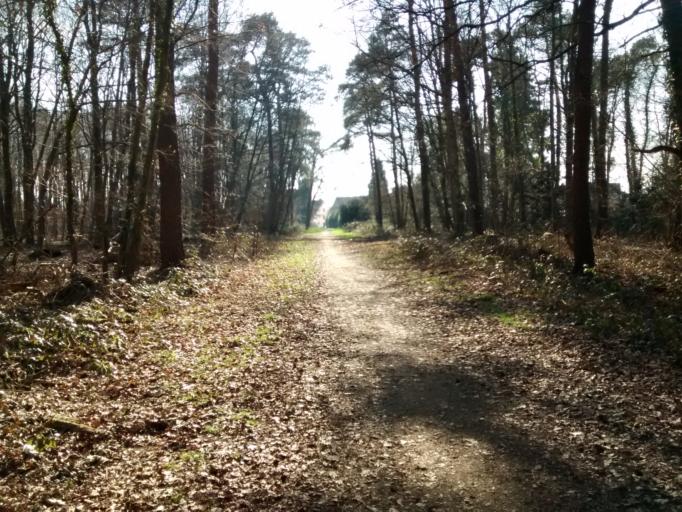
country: DE
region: North Rhine-Westphalia
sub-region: Regierungsbezirk Koln
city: Merheim
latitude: 51.0022
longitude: 7.0482
